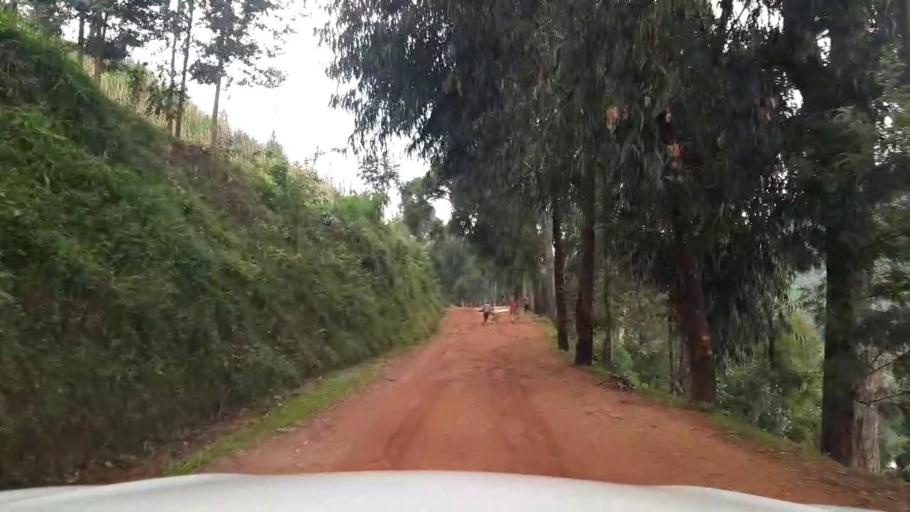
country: UG
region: Western Region
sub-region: Kisoro District
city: Kisoro
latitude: -1.4011
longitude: 29.8013
